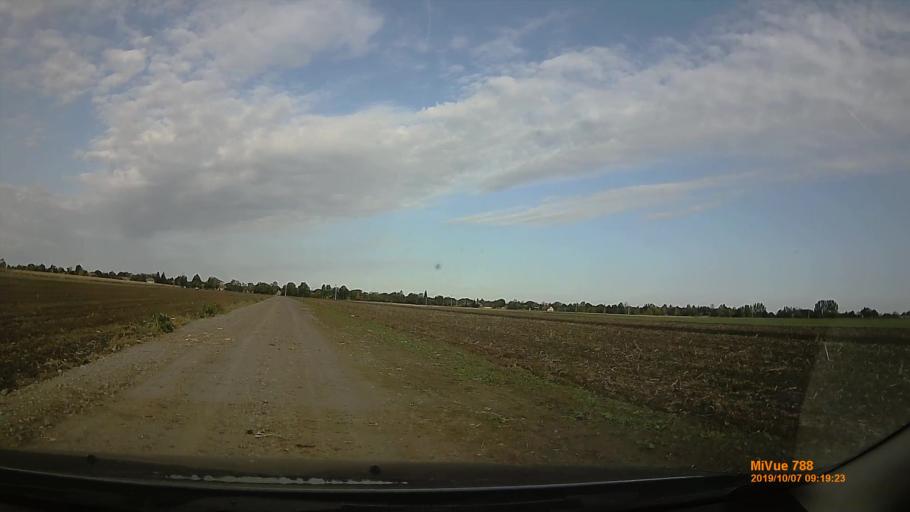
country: HU
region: Bekes
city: Szarvas
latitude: 46.8157
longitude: 20.6626
